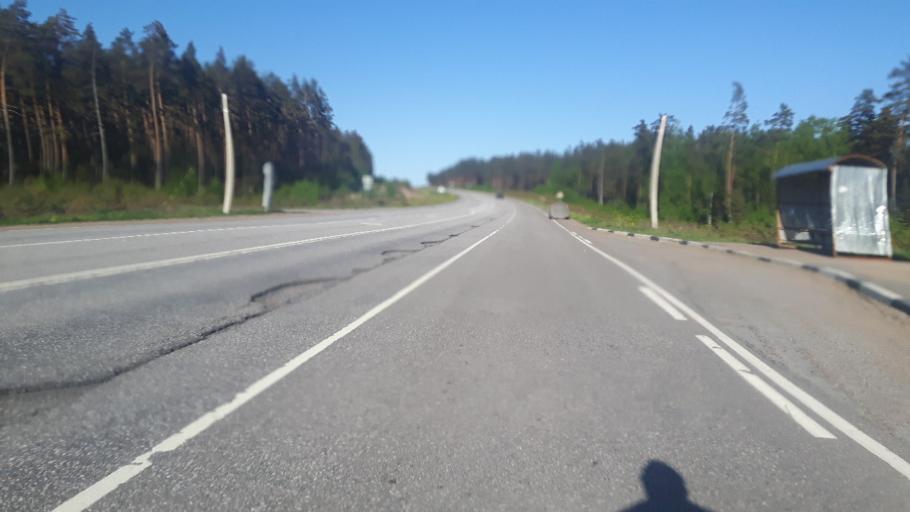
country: RU
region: Leningrad
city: Molodezhnoye
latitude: 60.1677
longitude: 29.2593
